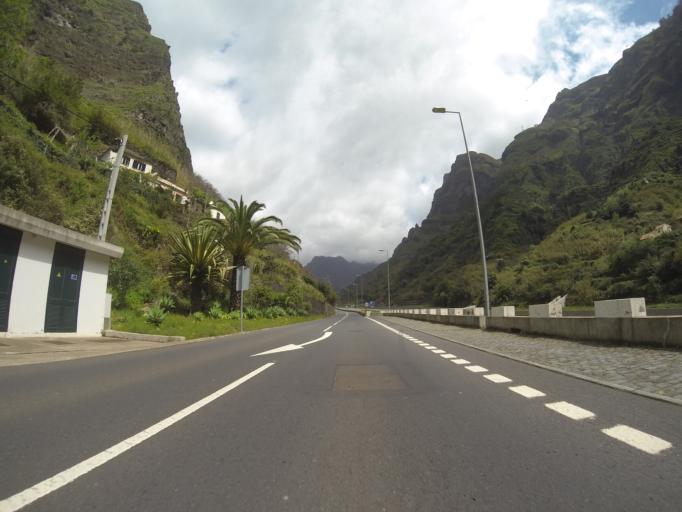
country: PT
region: Madeira
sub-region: Ribeira Brava
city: Campanario
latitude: 32.7133
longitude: -17.0345
